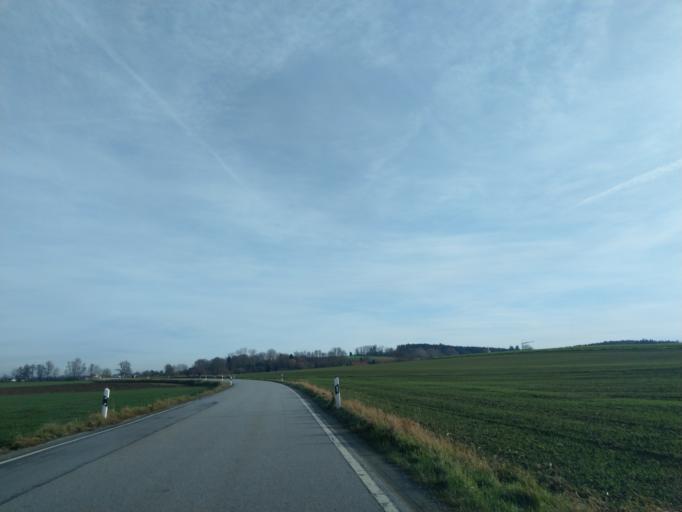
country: DE
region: Bavaria
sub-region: Lower Bavaria
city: Wallerfing
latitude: 48.6904
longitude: 12.8572
